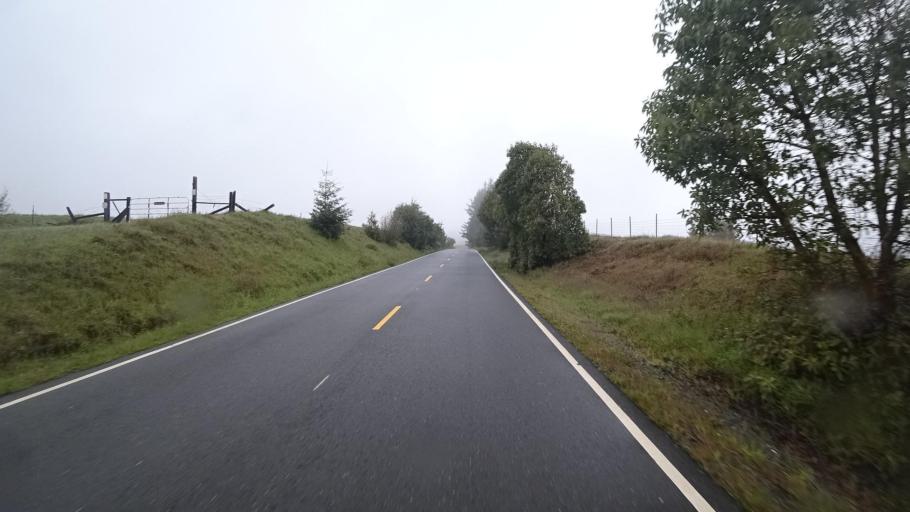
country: US
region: California
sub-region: Humboldt County
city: Westhaven-Moonstone
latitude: 41.1684
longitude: -123.9175
